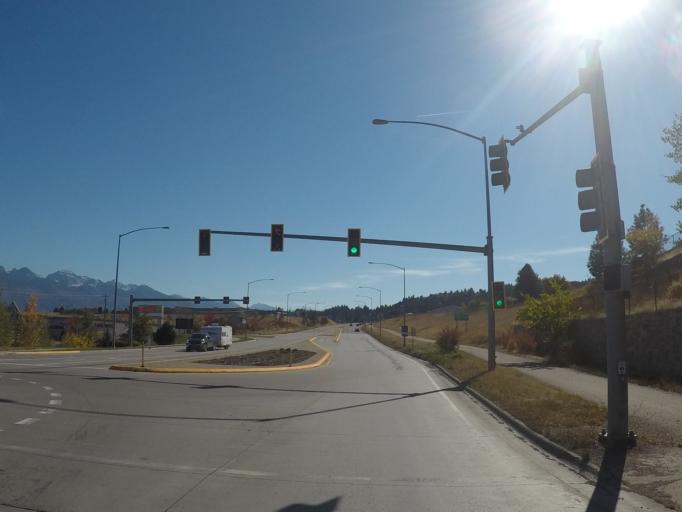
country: US
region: Montana
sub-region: Lake County
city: Polson
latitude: 47.6890
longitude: -114.1259
